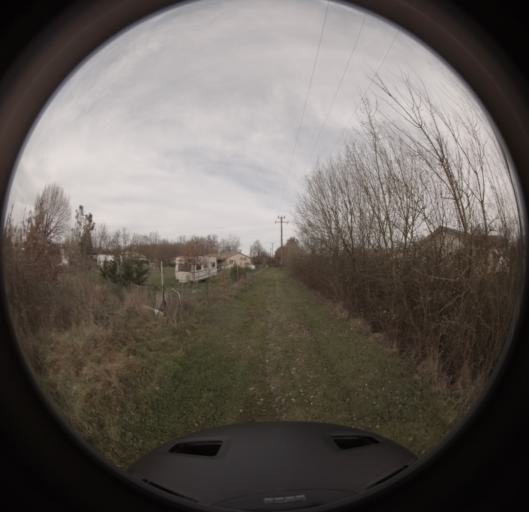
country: FR
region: Midi-Pyrenees
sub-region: Departement du Tarn-et-Garonne
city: Montbeton
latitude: 43.9973
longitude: 1.2811
